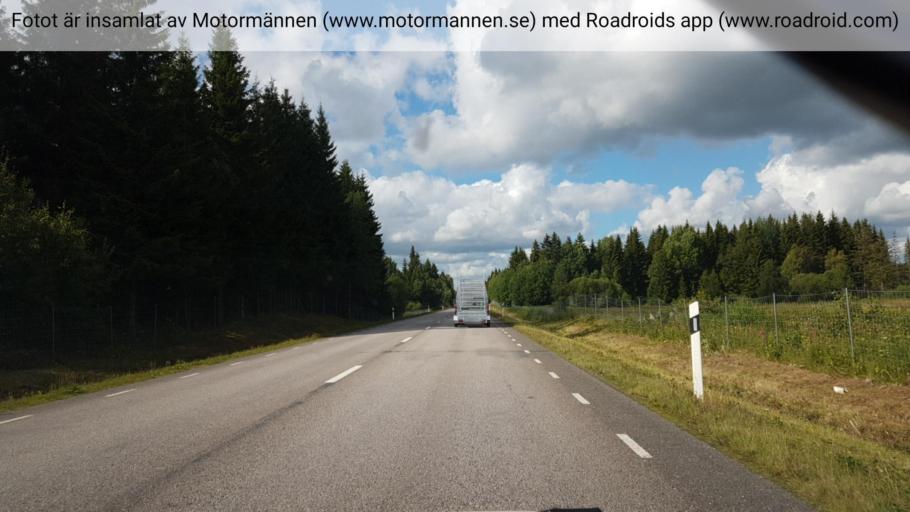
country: SE
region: Vaestra Goetaland
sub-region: Falkopings Kommun
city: Falkoeping
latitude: 58.0508
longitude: 13.5457
